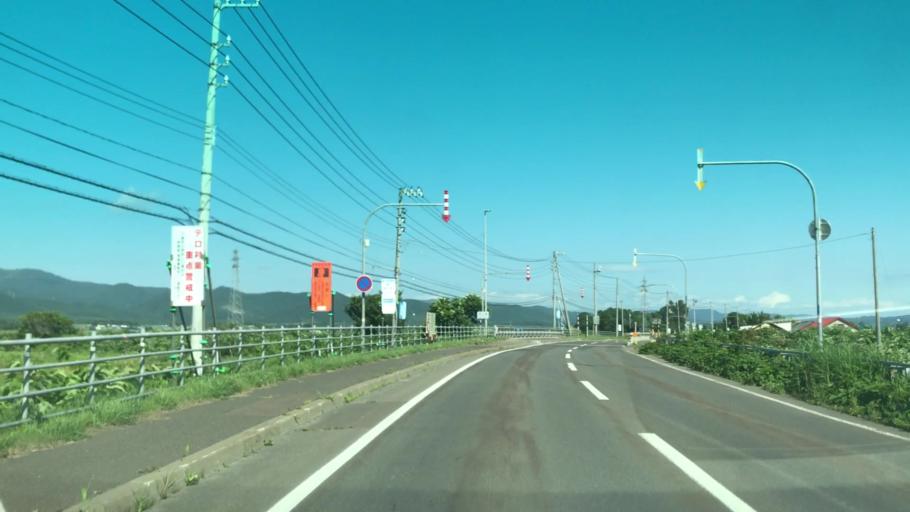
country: JP
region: Hokkaido
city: Iwanai
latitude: 43.0291
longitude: 140.5418
